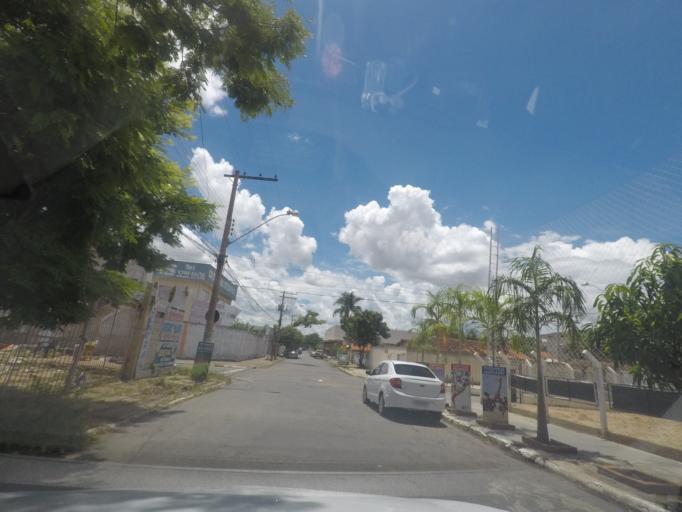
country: BR
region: Goias
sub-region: Goiania
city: Goiania
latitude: -16.6661
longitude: -49.2876
